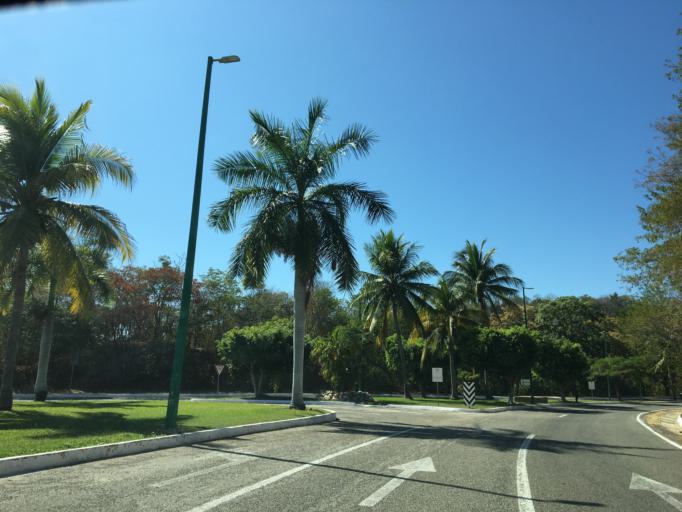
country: MX
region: Oaxaca
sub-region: Santa Maria Huatulco
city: Crucecita
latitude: 15.7734
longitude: -96.0819
